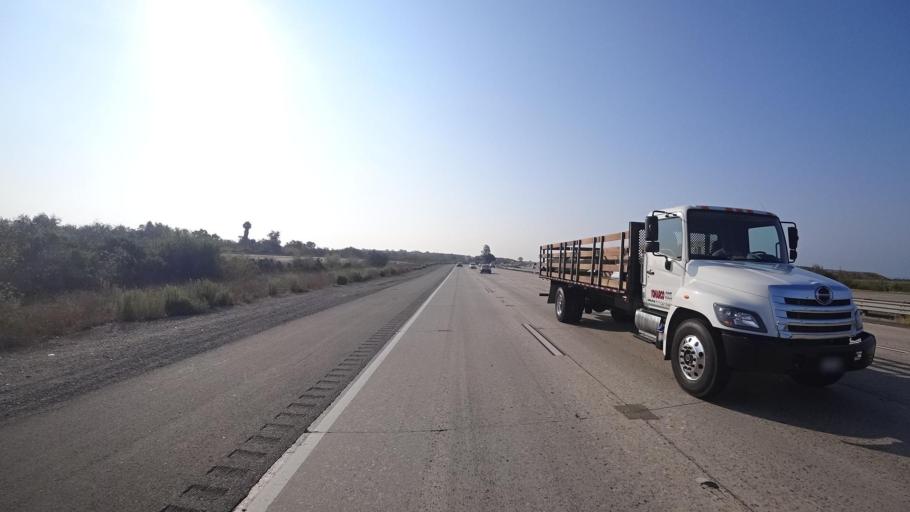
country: US
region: California
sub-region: San Diego County
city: Camp Pendleton South
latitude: 33.2955
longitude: -117.4601
